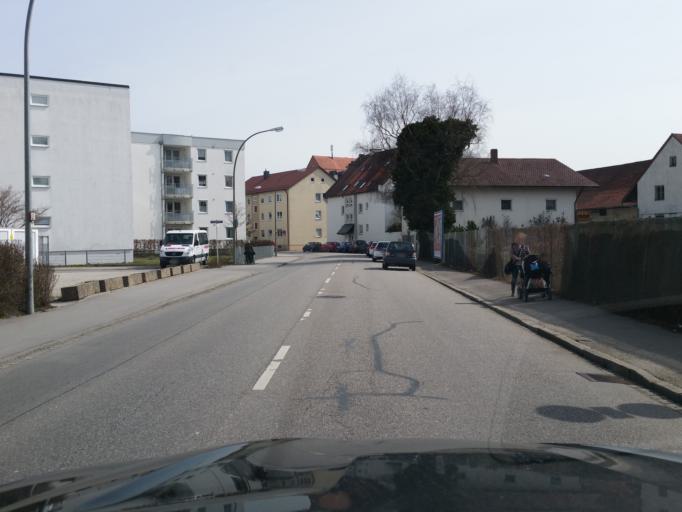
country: DE
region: Bavaria
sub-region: Lower Bavaria
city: Landshut
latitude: 48.5398
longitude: 12.1373
